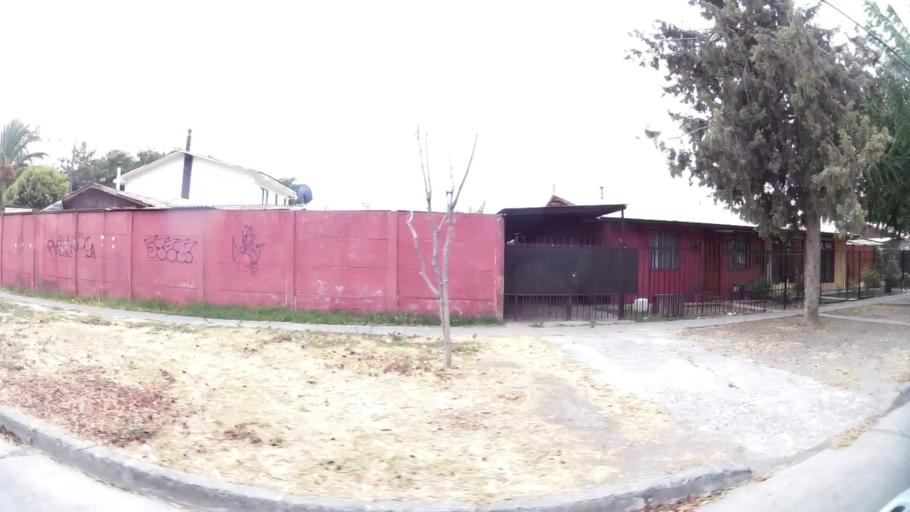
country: CL
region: O'Higgins
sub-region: Provincia de Cachapoal
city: Rancagua
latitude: -34.1519
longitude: -70.7296
